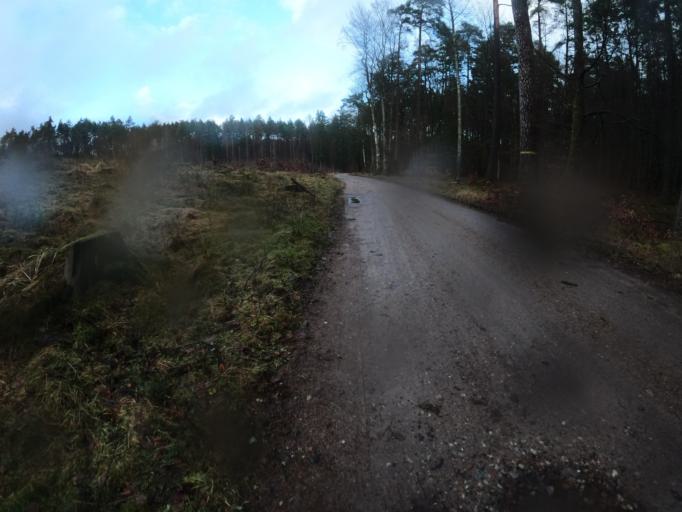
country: PL
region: West Pomeranian Voivodeship
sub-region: Powiat slawienski
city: Slawno
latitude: 54.2595
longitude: 16.7061
